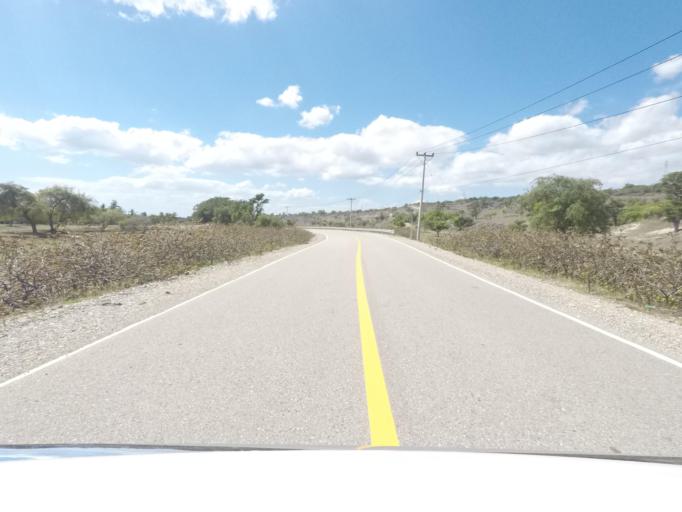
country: TL
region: Baucau
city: Baucau
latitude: -8.4377
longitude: 126.6650
